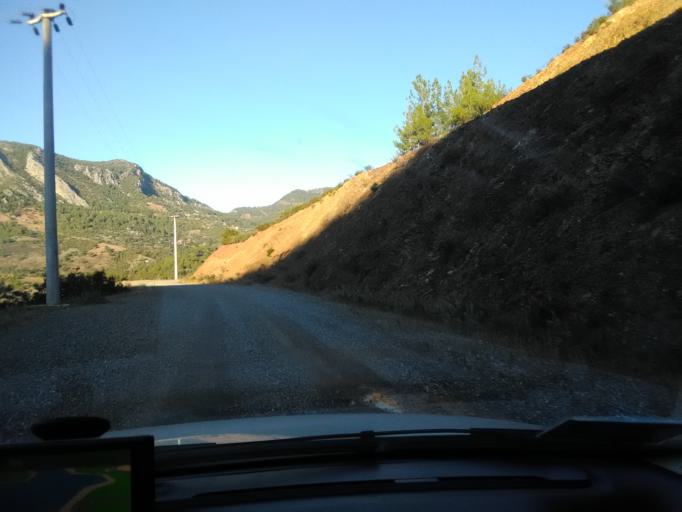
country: TR
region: Antalya
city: Gazipasa
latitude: 36.3131
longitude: 32.3935
